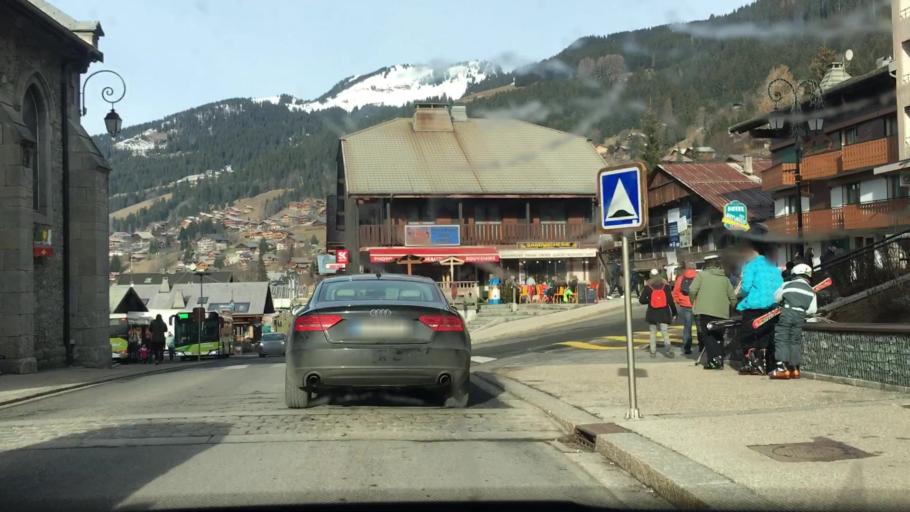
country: FR
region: Rhone-Alpes
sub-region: Departement de la Haute-Savoie
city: Chatel
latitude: 46.2675
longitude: 6.8410
